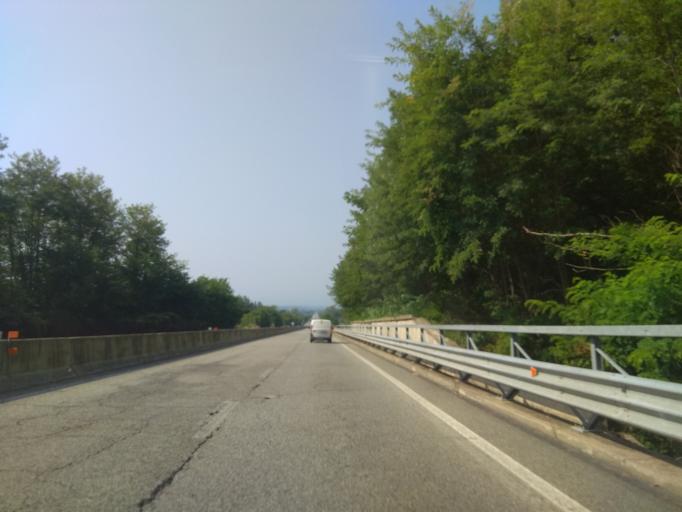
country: IT
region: Piedmont
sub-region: Provincia di Biella
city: Cossato
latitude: 45.5527
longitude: 8.2007
